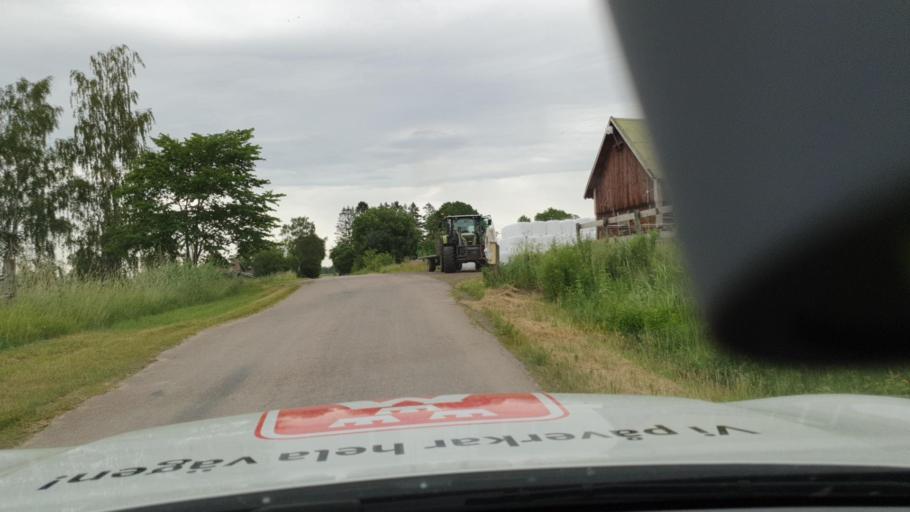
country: SE
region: Vaestra Goetaland
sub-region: Skovde Kommun
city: Skoevde
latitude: 58.3732
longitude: 13.8868
